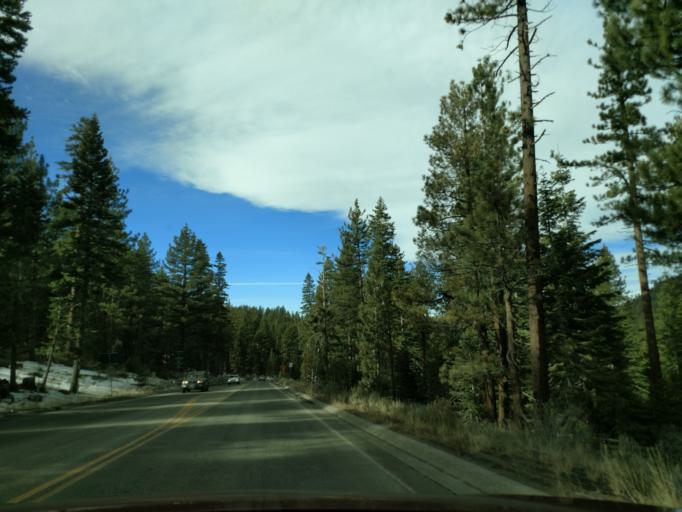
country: US
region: Nevada
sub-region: Douglas County
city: Kingsbury
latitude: 39.1065
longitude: -119.9194
